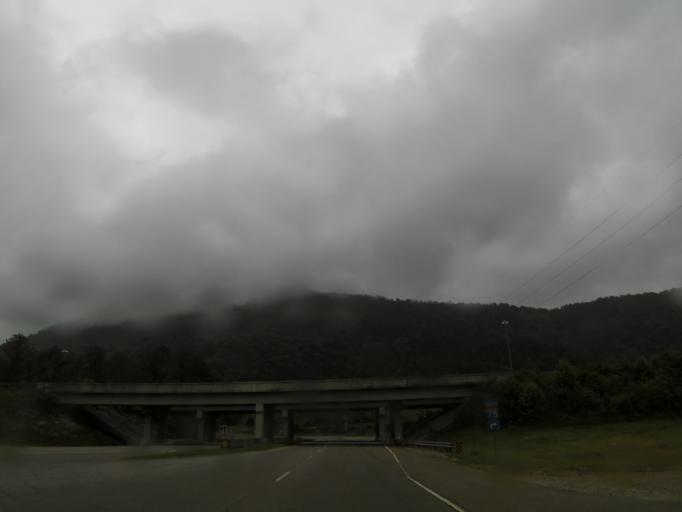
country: US
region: Tennessee
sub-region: Campbell County
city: Jellico
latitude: 36.5797
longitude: -84.1122
